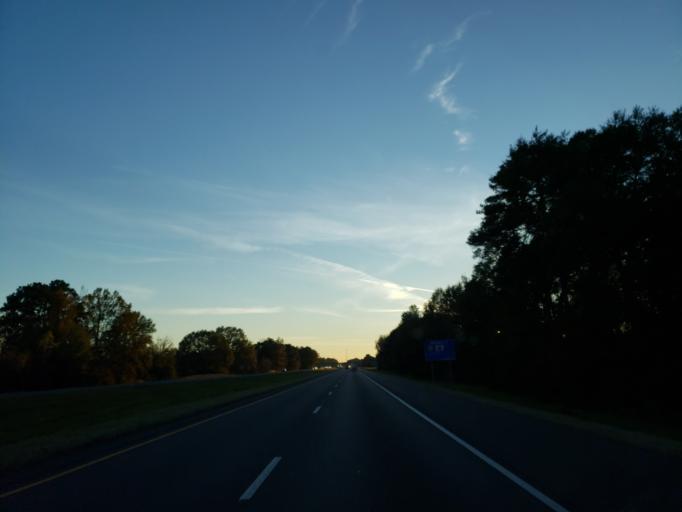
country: US
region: Alabama
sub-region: Greene County
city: Eutaw
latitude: 32.8015
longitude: -88.0249
